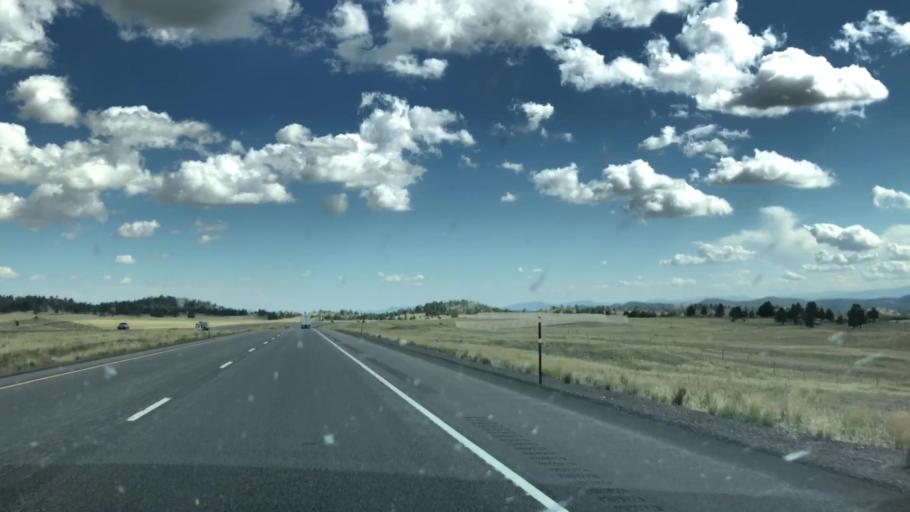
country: US
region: Wyoming
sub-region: Albany County
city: Laramie
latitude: 41.0238
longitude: -105.4256
